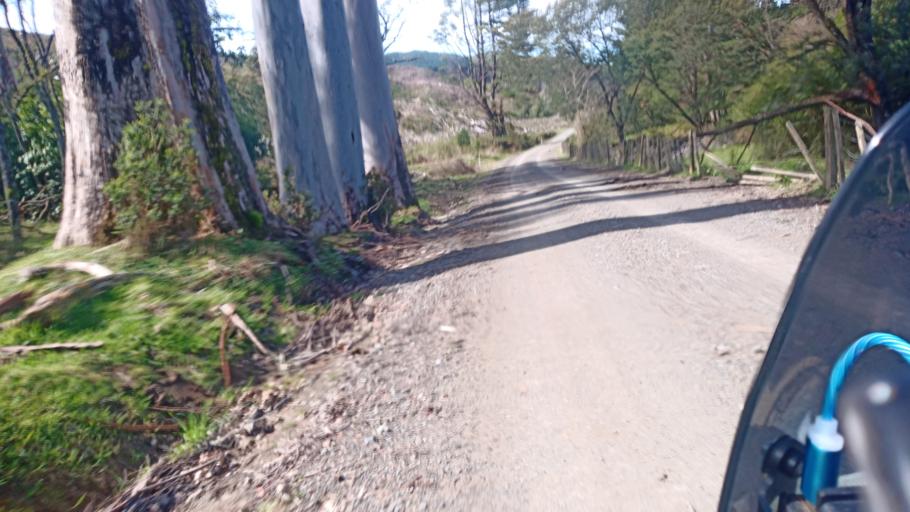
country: NZ
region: Gisborne
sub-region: Gisborne District
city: Gisborne
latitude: -37.8530
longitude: 178.0785
